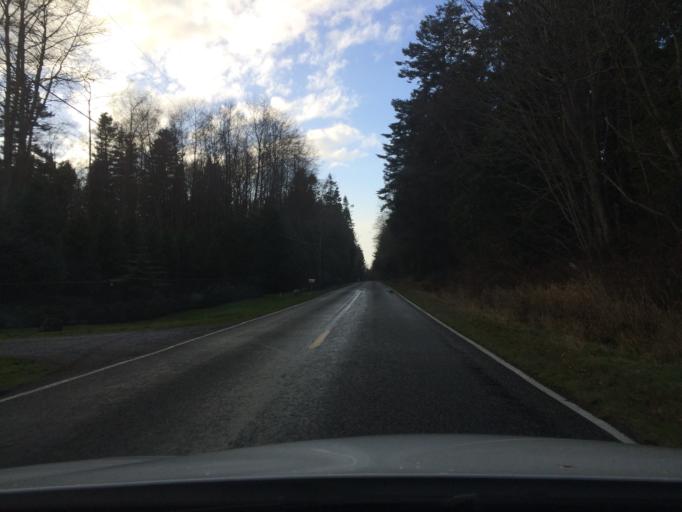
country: US
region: Washington
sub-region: Whatcom County
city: Birch Bay
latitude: 48.9405
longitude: -122.8118
